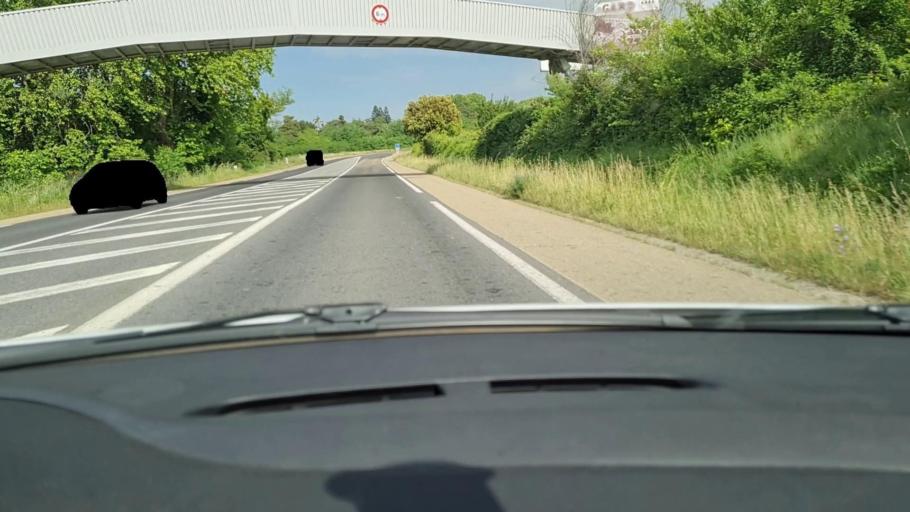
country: FR
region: Languedoc-Roussillon
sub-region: Departement du Gard
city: Bellegarde
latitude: 43.7625
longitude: 4.4790
